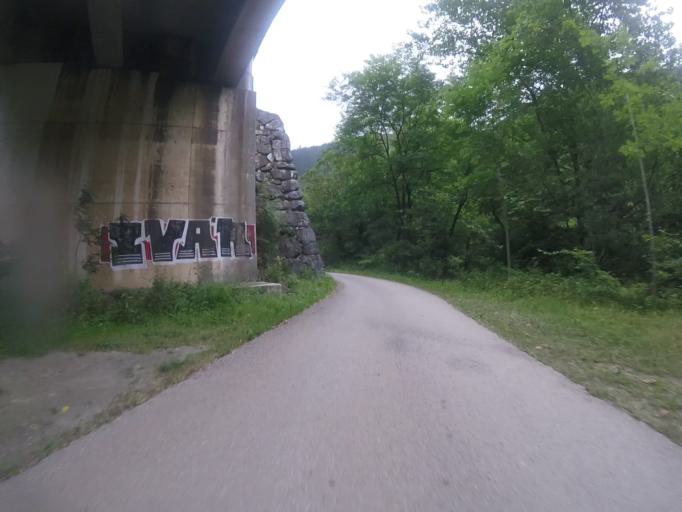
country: ES
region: Navarre
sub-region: Provincia de Navarra
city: Igantzi
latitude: 43.2140
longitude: -1.6719
